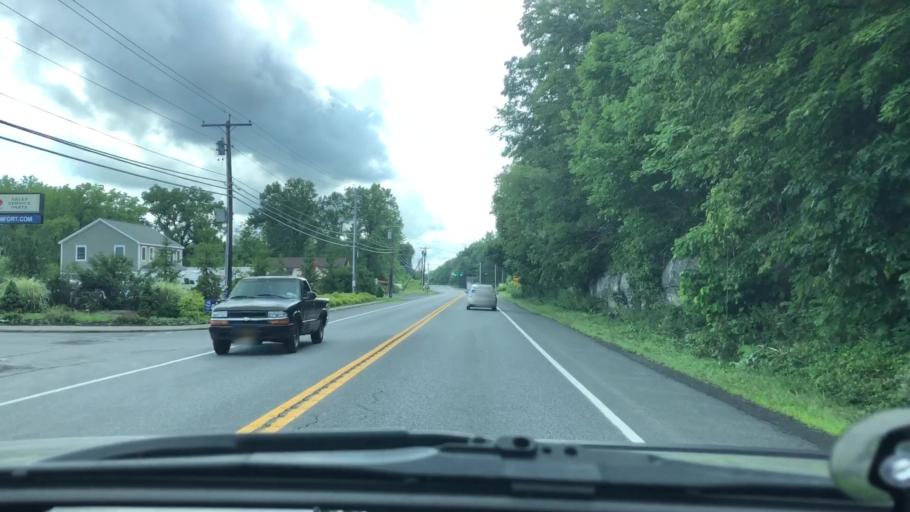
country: US
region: New York
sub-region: Ulster County
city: Saugerties
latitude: 42.0977
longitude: -73.9713
